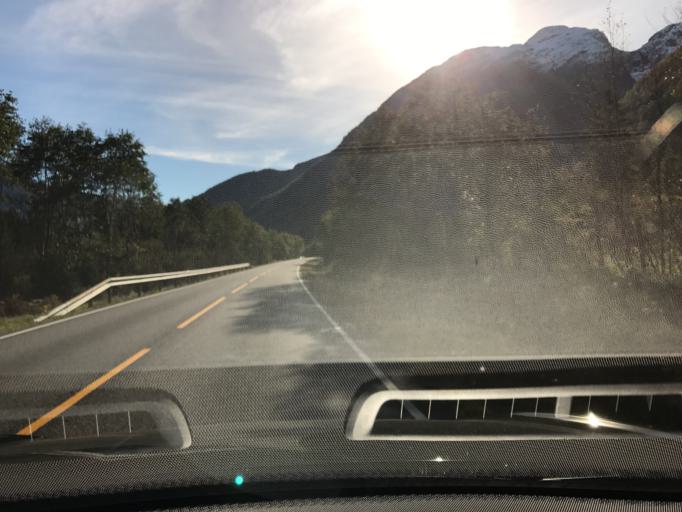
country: NO
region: Sogn og Fjordane
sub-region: Jolster
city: Skei
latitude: 61.4603
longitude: 6.7410
